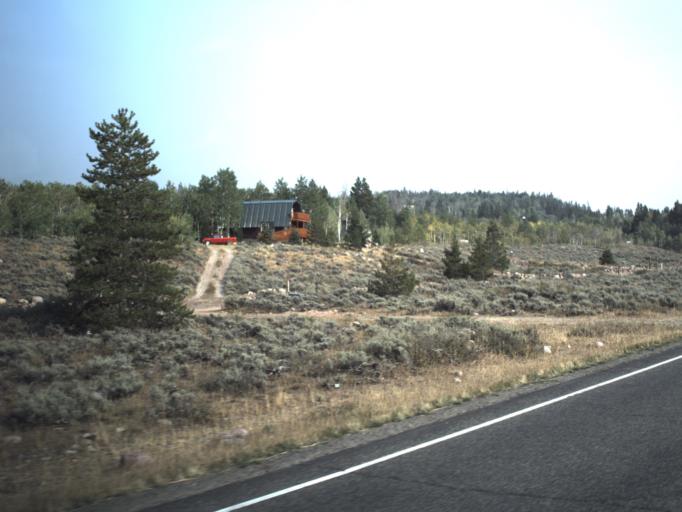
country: US
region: Wyoming
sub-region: Uinta County
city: Evanston
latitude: 40.9366
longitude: -110.8357
